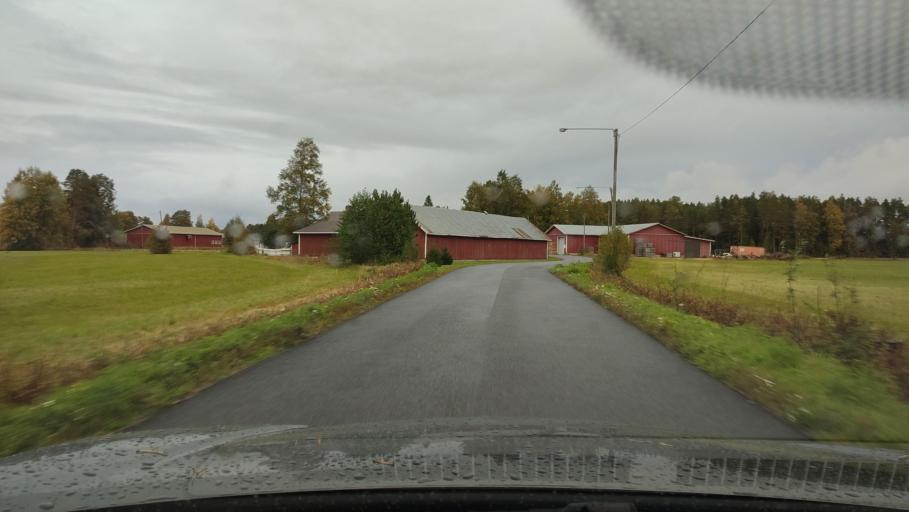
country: FI
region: Southern Ostrobothnia
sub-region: Suupohja
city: Karijoki
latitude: 62.2261
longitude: 21.6459
